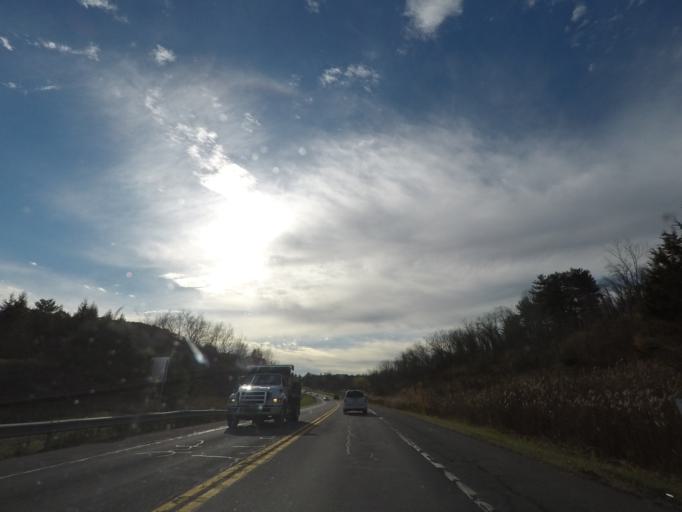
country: US
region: New York
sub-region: Albany County
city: McKownville
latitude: 42.6522
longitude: -73.8436
